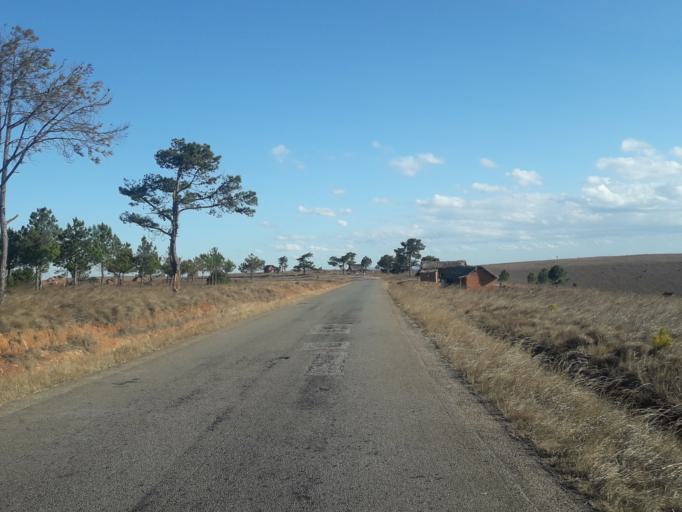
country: MG
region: Analamanga
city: Ankazobe
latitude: -17.8866
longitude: 47.0850
